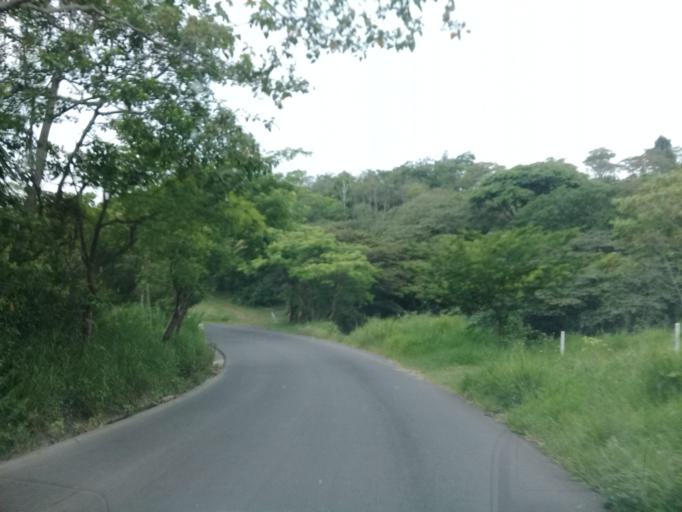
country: MX
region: Veracruz
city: El Castillo
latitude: 19.5576
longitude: -96.8534
